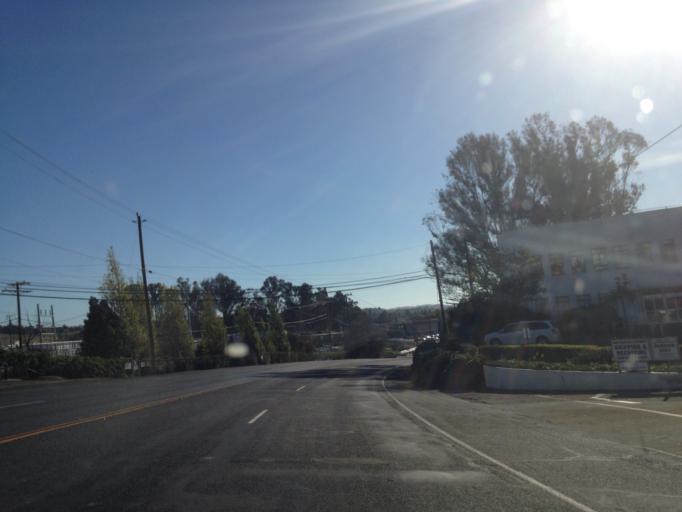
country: US
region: California
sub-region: Contra Costa County
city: Rodeo
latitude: 38.0462
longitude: -122.2578
